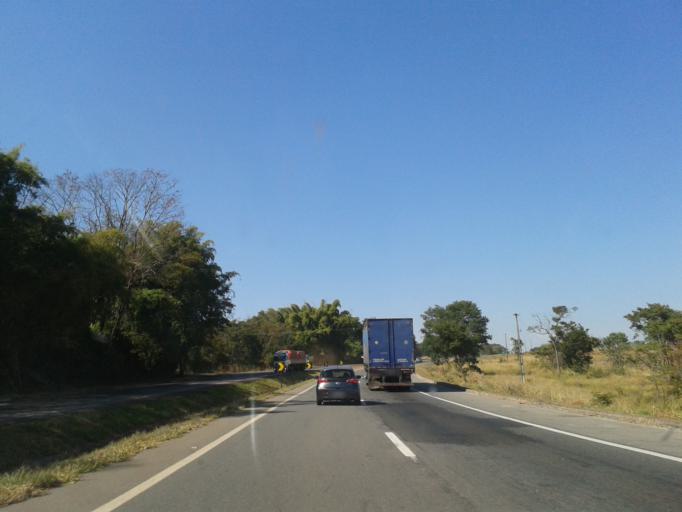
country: BR
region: Goias
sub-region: Piracanjuba
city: Piracanjuba
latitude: -17.2778
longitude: -49.2372
